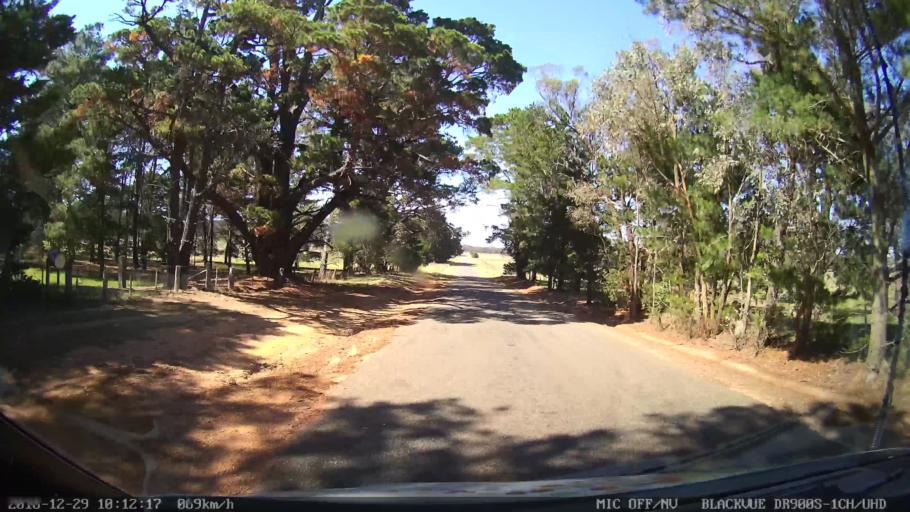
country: AU
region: New South Wales
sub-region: Yass Valley
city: Gundaroo
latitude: -34.8921
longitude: 149.4489
